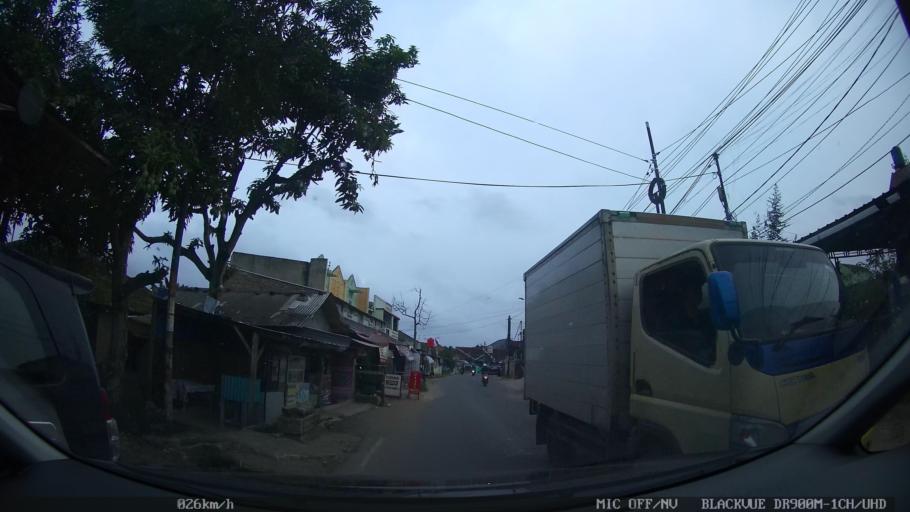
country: ID
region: Lampung
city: Kedaton
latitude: -5.4008
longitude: 105.2697
